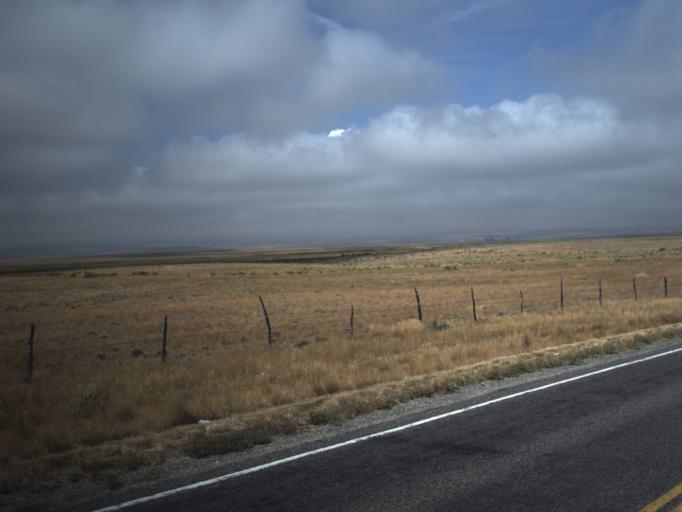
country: US
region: Utah
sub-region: Rich County
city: Randolph
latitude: 41.4610
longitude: -111.0992
